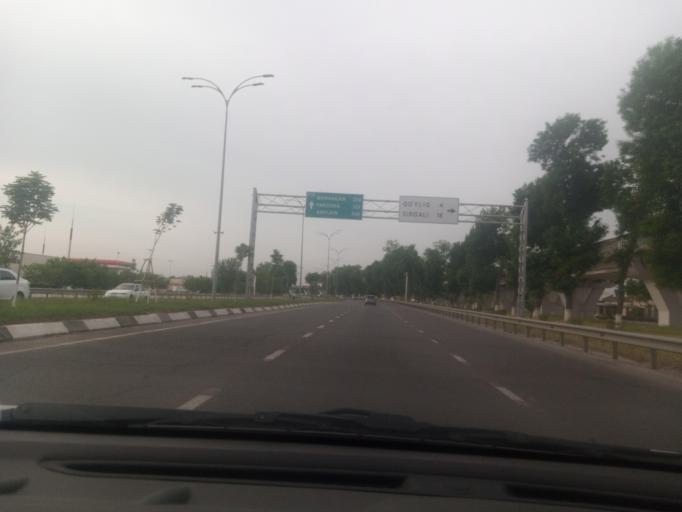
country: UZ
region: Toshkent Shahri
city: Bektemir
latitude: 41.2740
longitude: 69.3620
